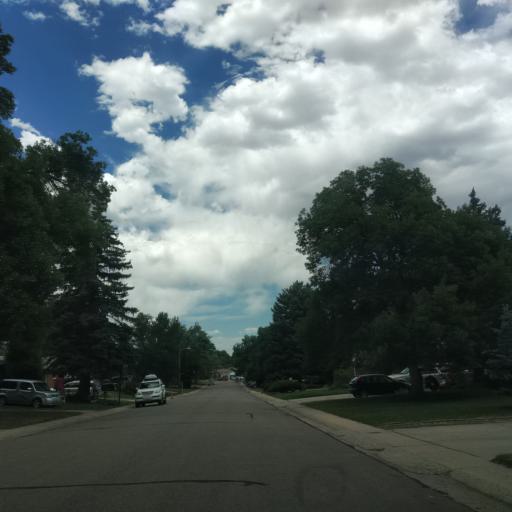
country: US
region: Colorado
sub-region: Jefferson County
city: Lakewood
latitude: 39.6865
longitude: -105.0871
